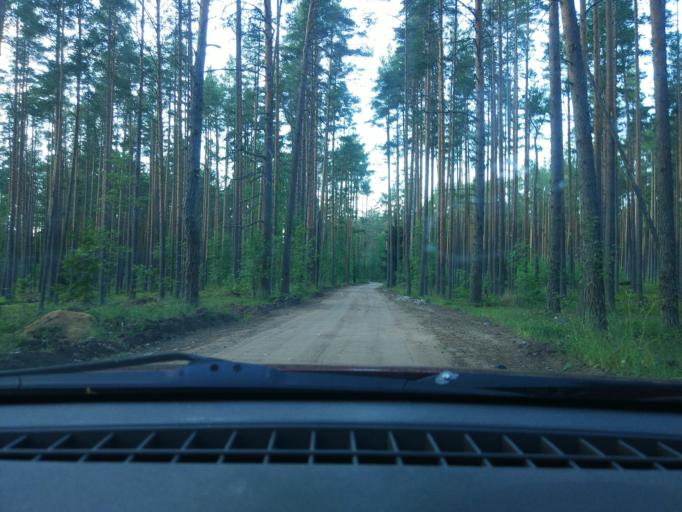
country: RU
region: Leningrad
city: Priozersk
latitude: 60.9272
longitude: 30.0551
